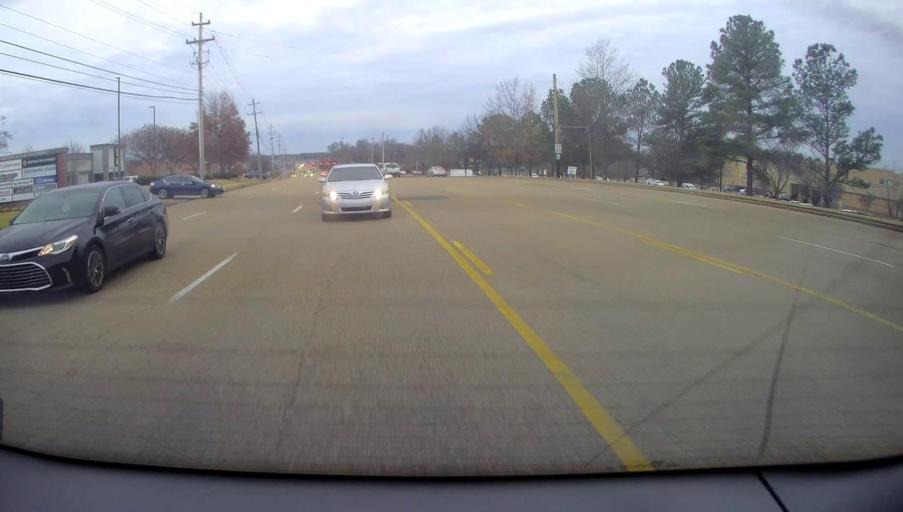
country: US
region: Tennessee
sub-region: Shelby County
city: Germantown
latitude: 35.0468
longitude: -89.7959
